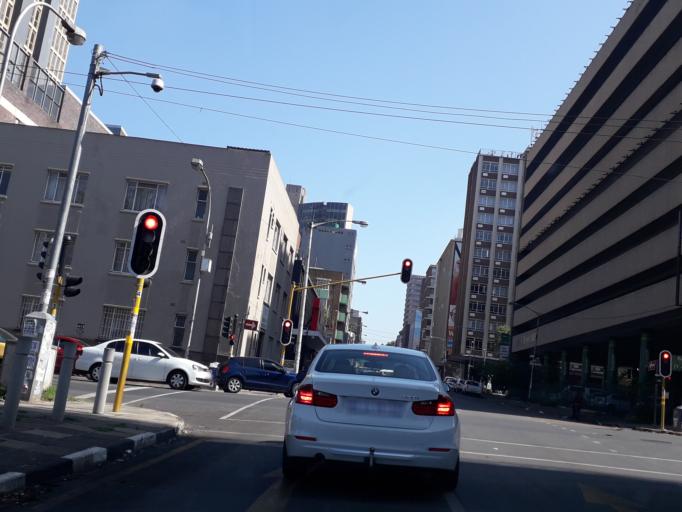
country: ZA
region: Gauteng
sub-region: City of Johannesburg Metropolitan Municipality
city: Johannesburg
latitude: -26.1952
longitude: 28.0361
